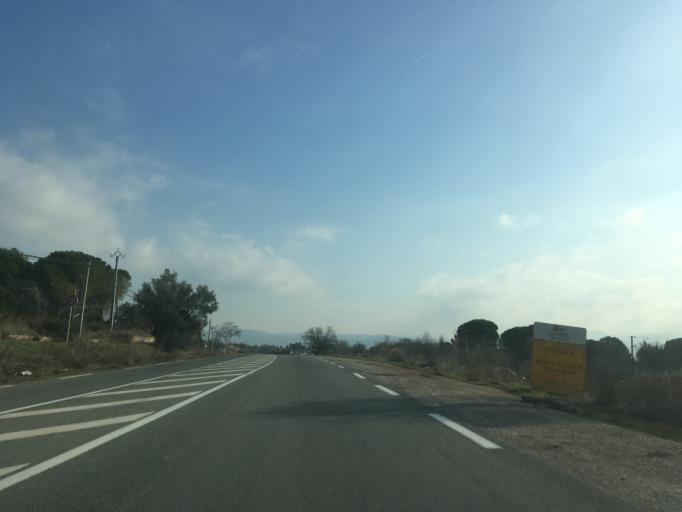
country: FR
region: Provence-Alpes-Cote d'Azur
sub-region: Departement du Var
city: Le Cannet-des-Maures
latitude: 43.4033
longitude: 6.3894
